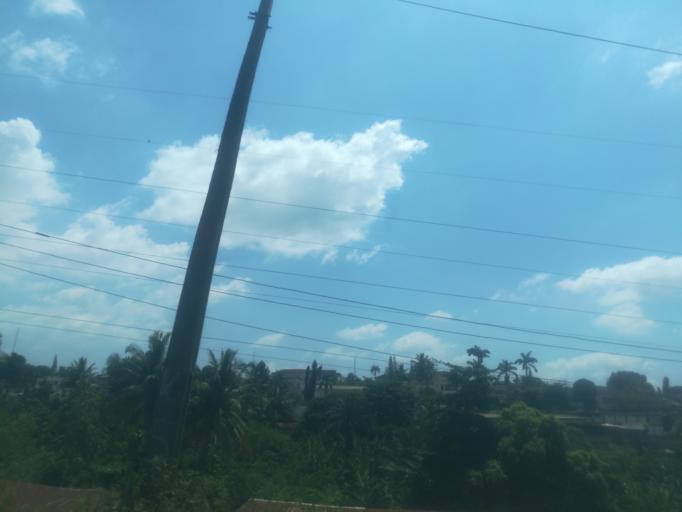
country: NG
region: Oyo
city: Ibadan
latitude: 7.3803
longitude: 3.8645
